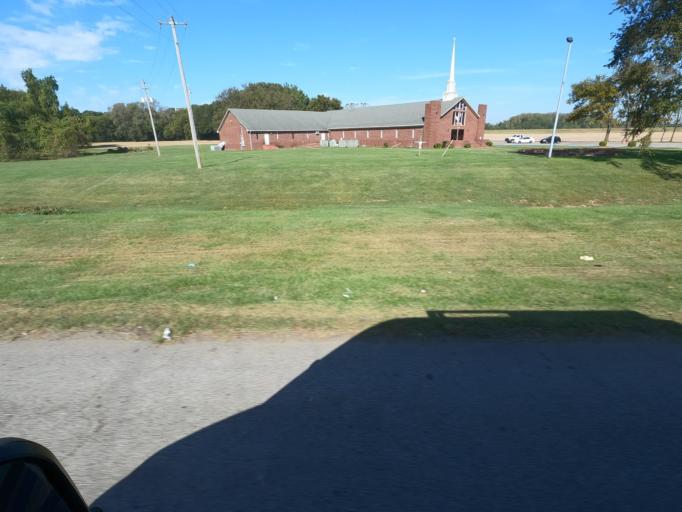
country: US
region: Tennessee
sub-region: Shelby County
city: Millington
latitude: 35.3693
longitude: -89.8845
